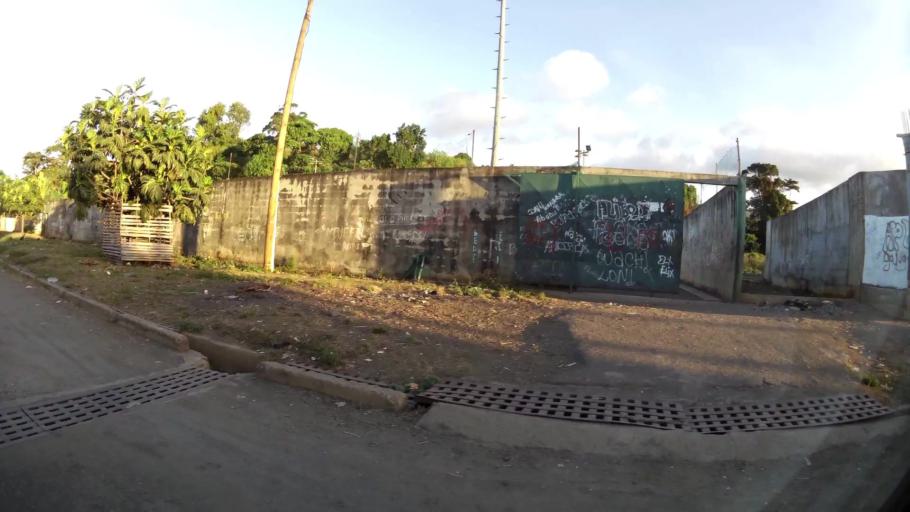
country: YT
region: Dembeni
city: Dembeni
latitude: -12.8452
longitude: 45.1919
